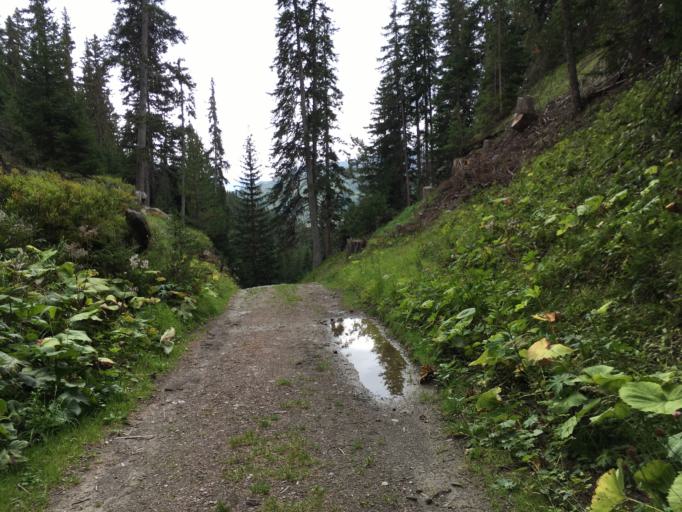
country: CH
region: Grisons
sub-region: Maloja District
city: Silvaplana
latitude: 46.4851
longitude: 9.6495
